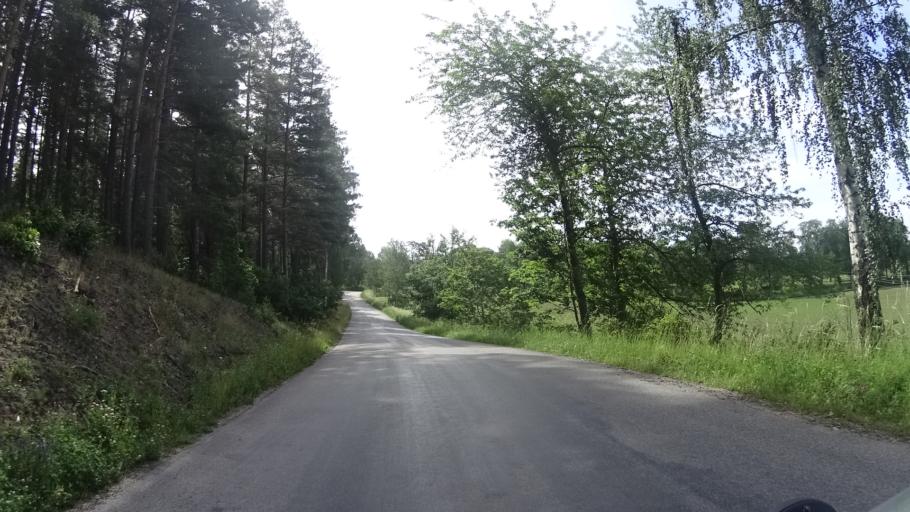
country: SE
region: Kalmar
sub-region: Vasterviks Kommun
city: Overum
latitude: 57.8742
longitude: 16.1744
